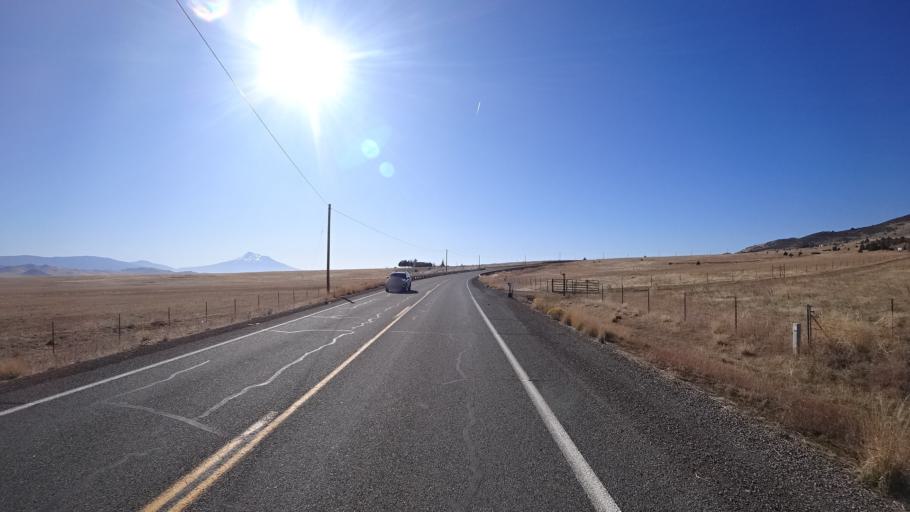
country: US
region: California
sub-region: Siskiyou County
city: Montague
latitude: 41.8094
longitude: -122.4984
